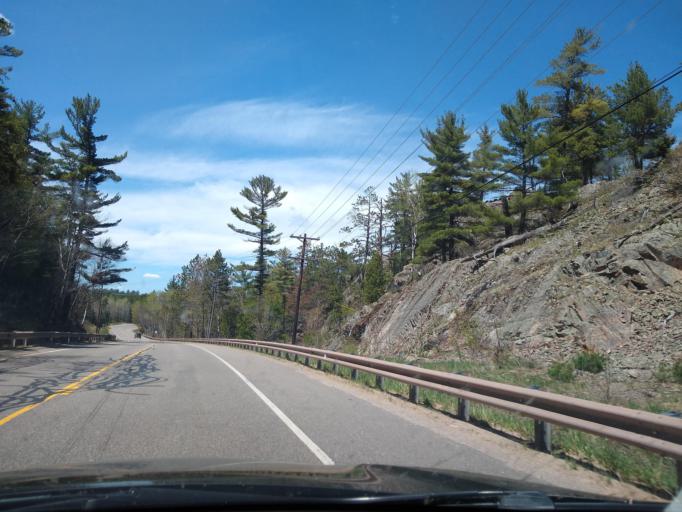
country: US
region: Michigan
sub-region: Marquette County
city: Trowbridge Park
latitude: 46.6050
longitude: -87.4628
